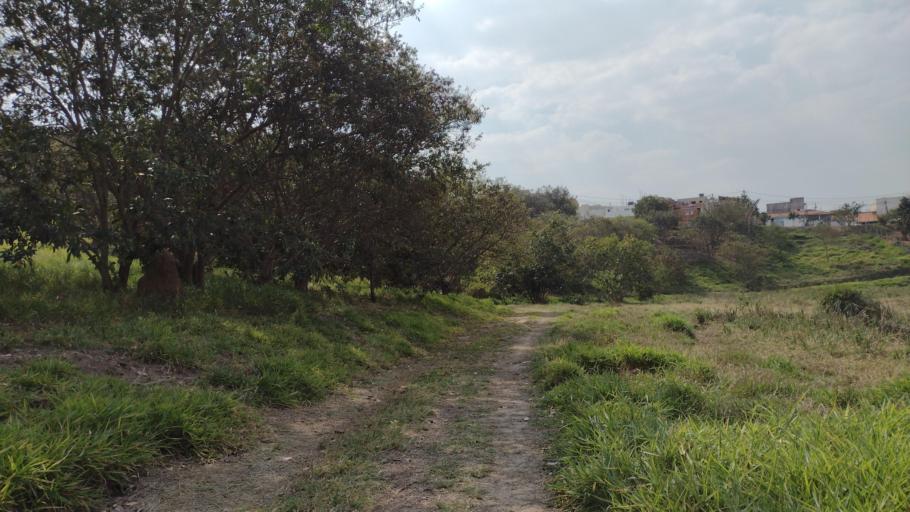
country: BR
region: Sao Paulo
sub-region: Sorocaba
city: Sorocaba
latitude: -23.4395
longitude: -47.4626
